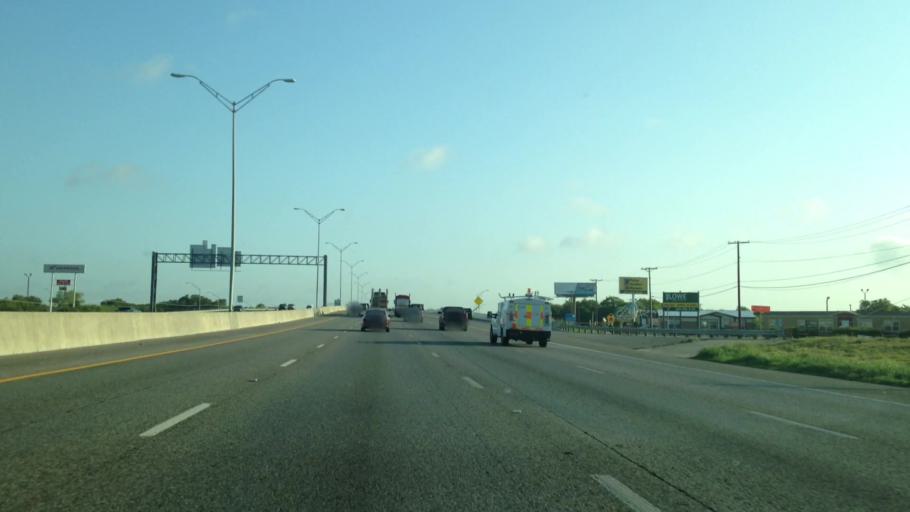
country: US
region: Texas
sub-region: Comal County
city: New Braunfels
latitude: 29.7099
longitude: -98.0892
